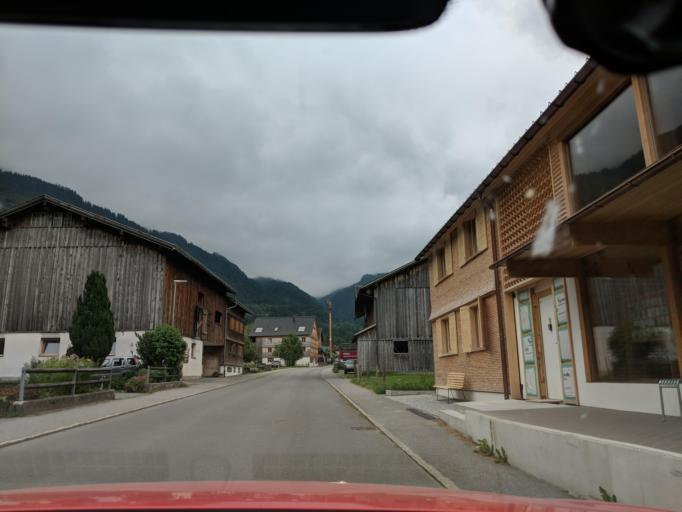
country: AT
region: Vorarlberg
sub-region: Politischer Bezirk Bregenz
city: Bezau
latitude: 47.3859
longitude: 9.9057
